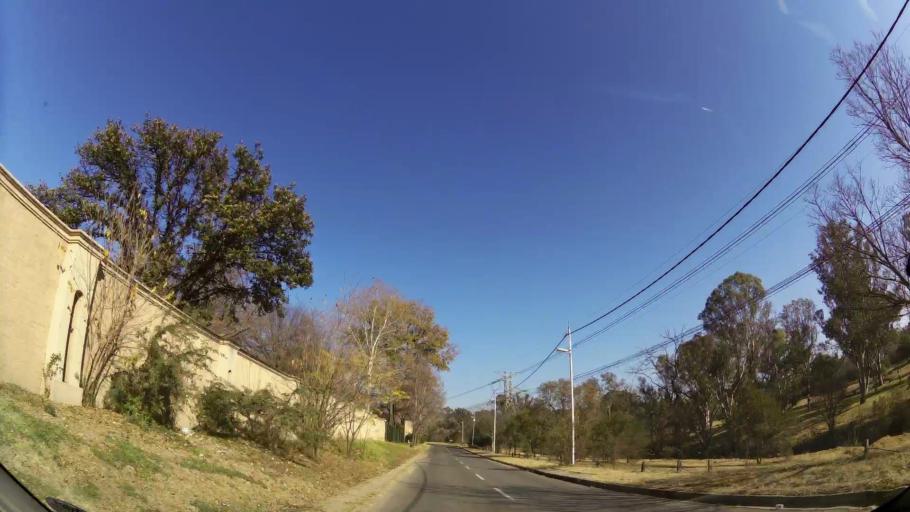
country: ZA
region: Gauteng
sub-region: City of Johannesburg Metropolitan Municipality
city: Midrand
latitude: -26.0617
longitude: 28.0467
